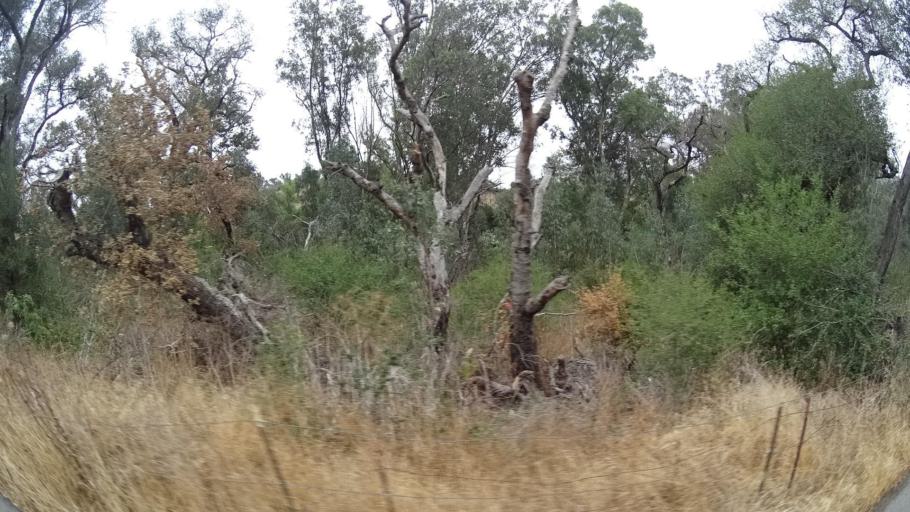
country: US
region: California
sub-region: San Diego County
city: San Marcos
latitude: 33.0964
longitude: -117.1382
